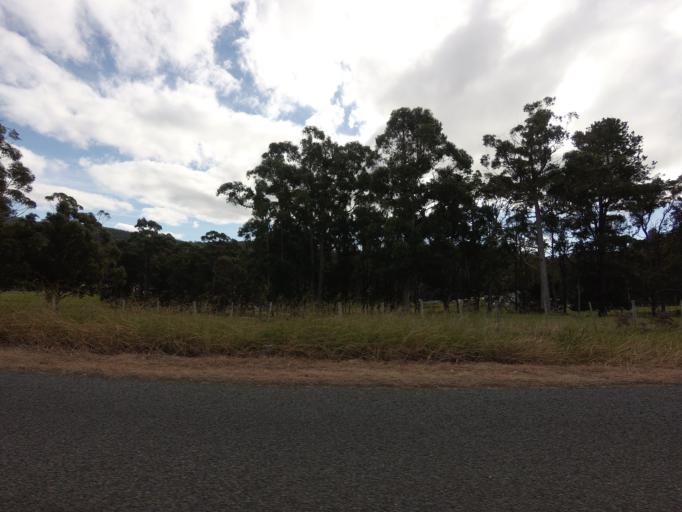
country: AU
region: Tasmania
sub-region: Clarence
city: Sandford
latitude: -43.0804
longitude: 147.7415
